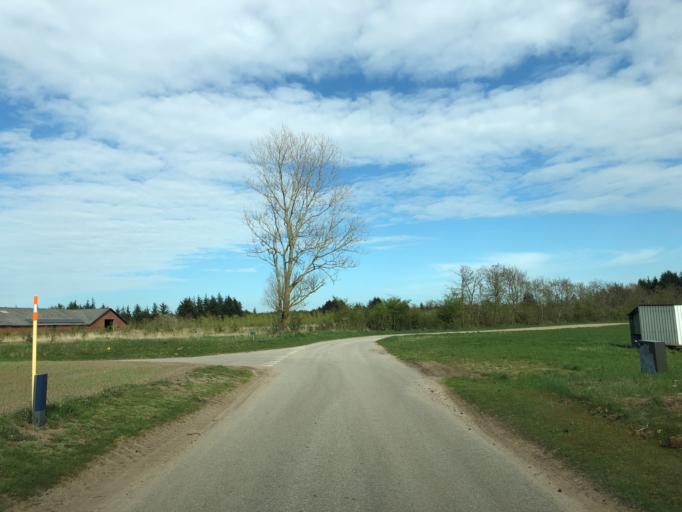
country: DK
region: Central Jutland
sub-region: Holstebro Kommune
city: Ulfborg
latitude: 56.2520
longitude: 8.3267
